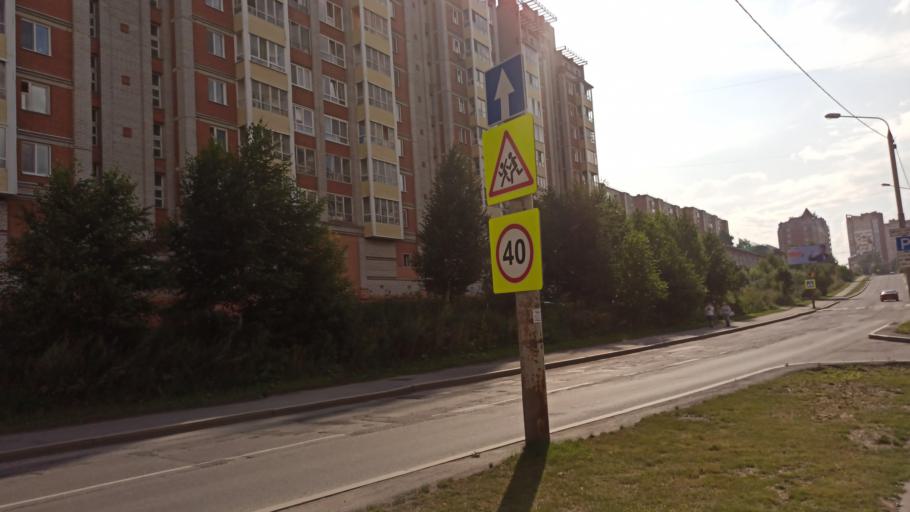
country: RU
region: Tomsk
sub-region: Tomskiy Rayon
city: Tomsk
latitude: 56.4825
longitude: 85.0134
